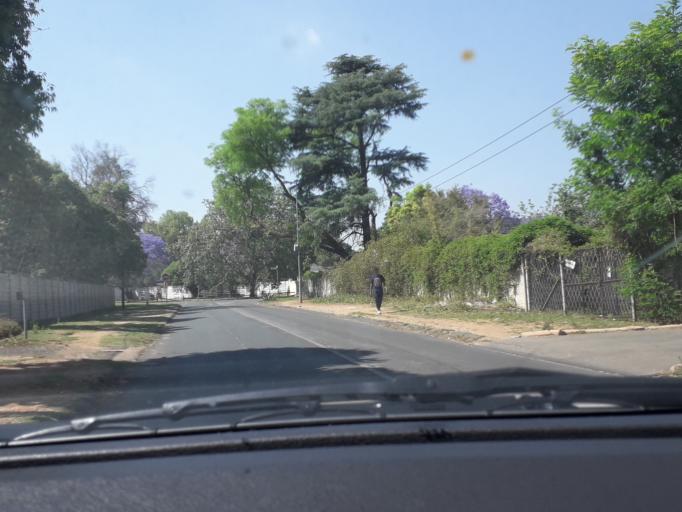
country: ZA
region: Gauteng
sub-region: City of Johannesburg Metropolitan Municipality
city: Johannesburg
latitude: -26.1198
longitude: 28.0780
